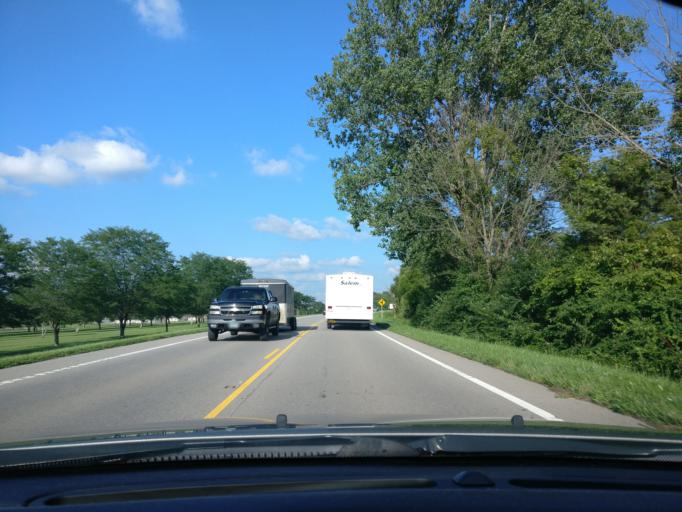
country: US
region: Ohio
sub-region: Warren County
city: Waynesville
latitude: 39.5204
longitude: -84.0661
